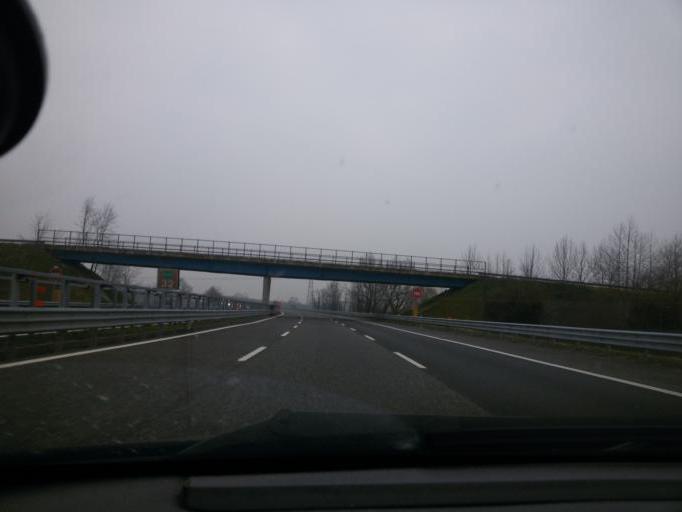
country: IT
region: Piedmont
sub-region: Provincia di Alessandria
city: Villanova Monferrato
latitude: 45.1797
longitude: 8.4964
